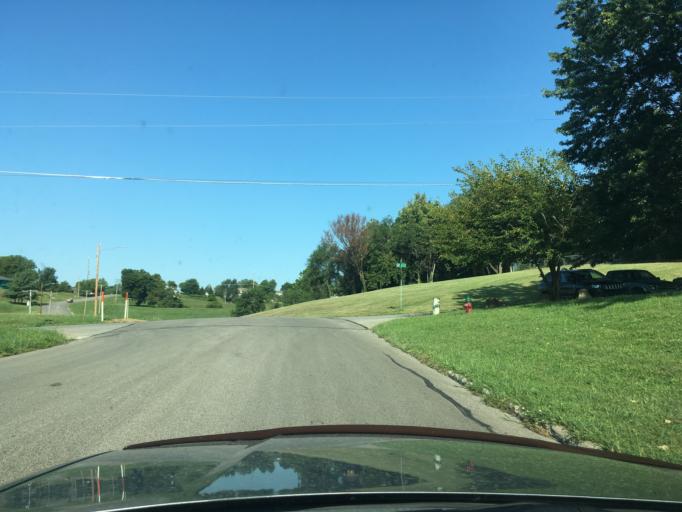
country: US
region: Kansas
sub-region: Atchison County
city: Atchison
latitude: 39.5786
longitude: -95.1200
